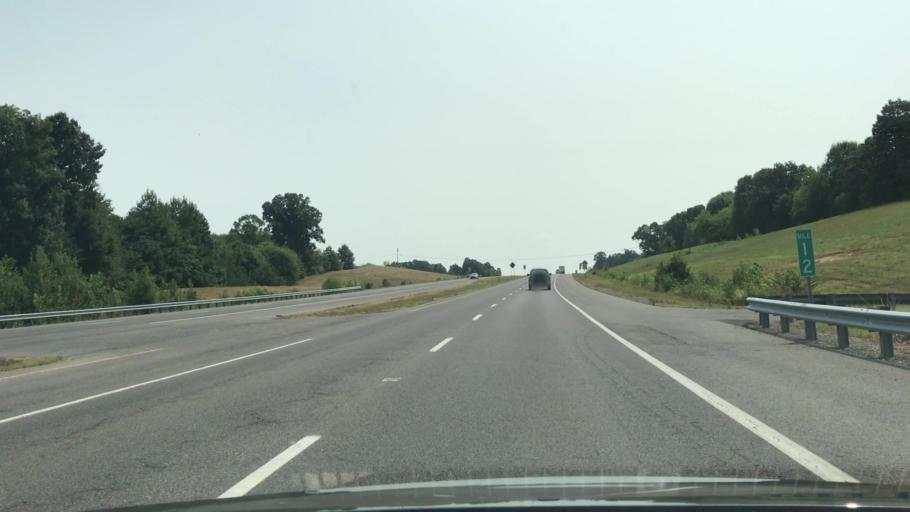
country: US
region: Kentucky
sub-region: Calloway County
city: Murray
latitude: 36.6514
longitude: -88.2766
